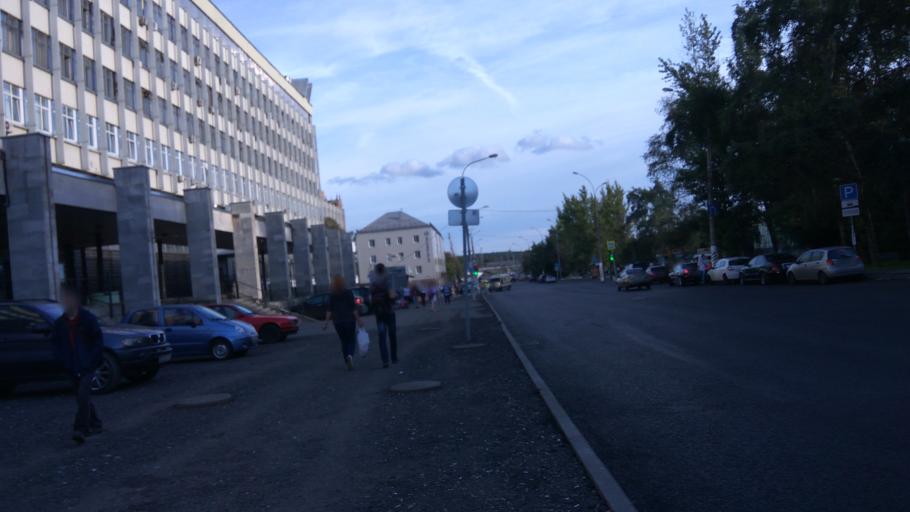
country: RU
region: Moscow
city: Orekhovo-Borisovo Severnoye
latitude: 55.6235
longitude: 37.6680
